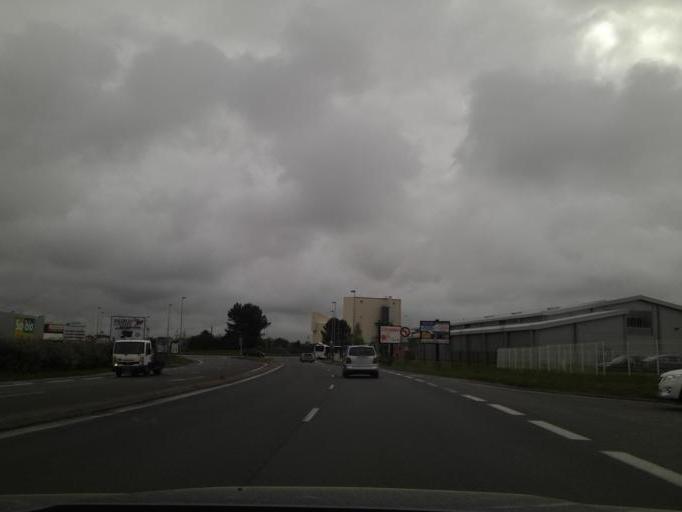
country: FR
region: Aquitaine
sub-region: Departement de la Gironde
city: Le Haillan
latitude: 44.8580
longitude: -0.6795
